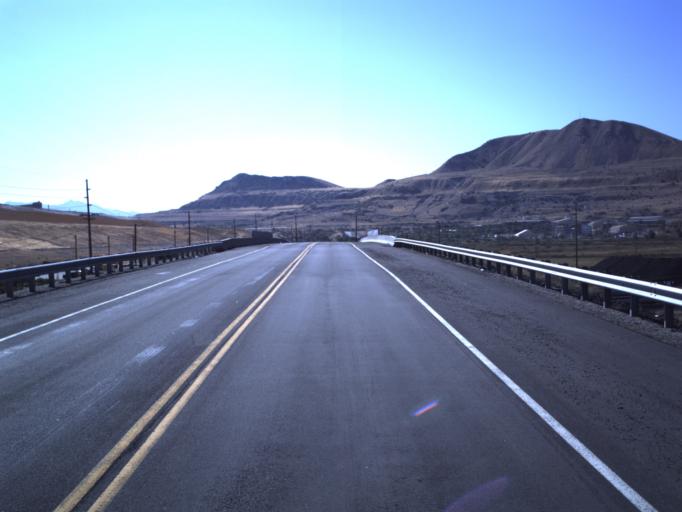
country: US
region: Utah
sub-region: Salt Lake County
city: Magna
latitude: 40.7418
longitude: -112.1788
